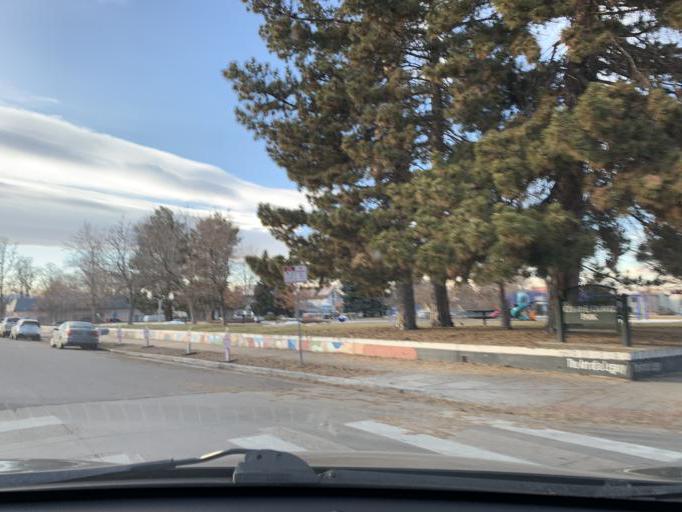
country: US
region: Colorado
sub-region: Jefferson County
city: Edgewater
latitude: 39.7729
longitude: -105.0441
